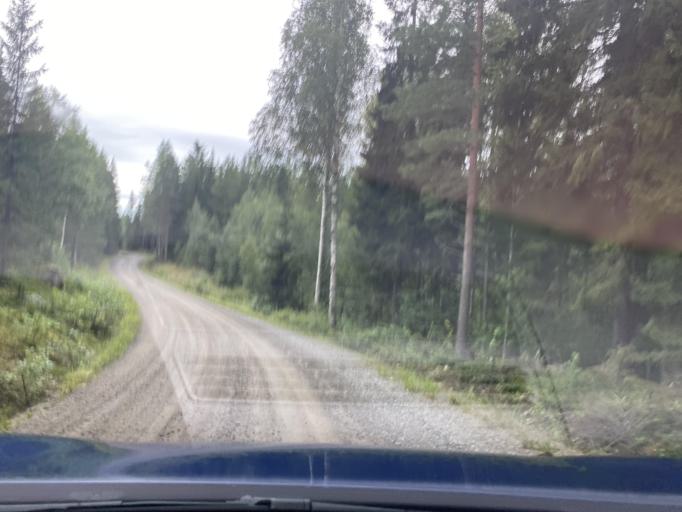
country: FI
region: Pirkanmaa
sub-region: Lounais-Pirkanmaa
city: Punkalaidun
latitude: 61.2431
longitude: 23.0447
